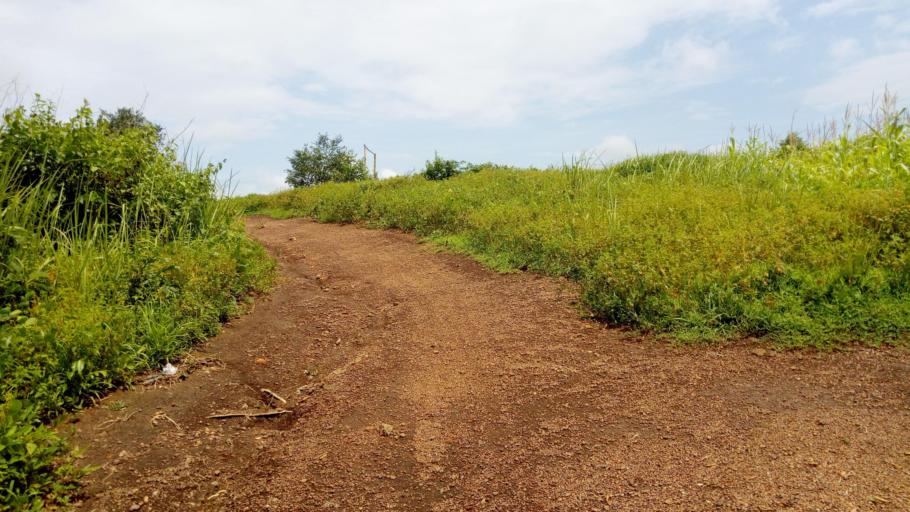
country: SL
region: Northern Province
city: Magburaka
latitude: 8.7197
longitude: -11.9619
